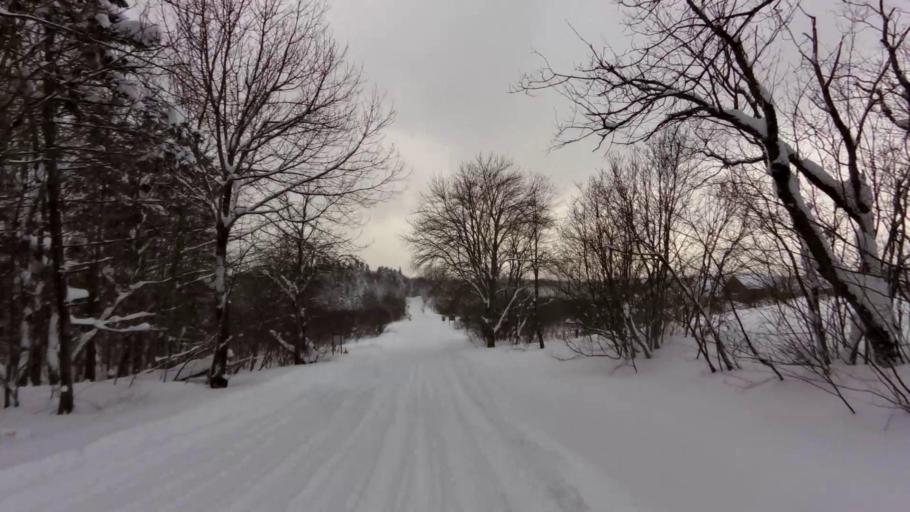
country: US
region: New York
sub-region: Lewis County
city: Lowville
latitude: 43.7323
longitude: -75.6676
